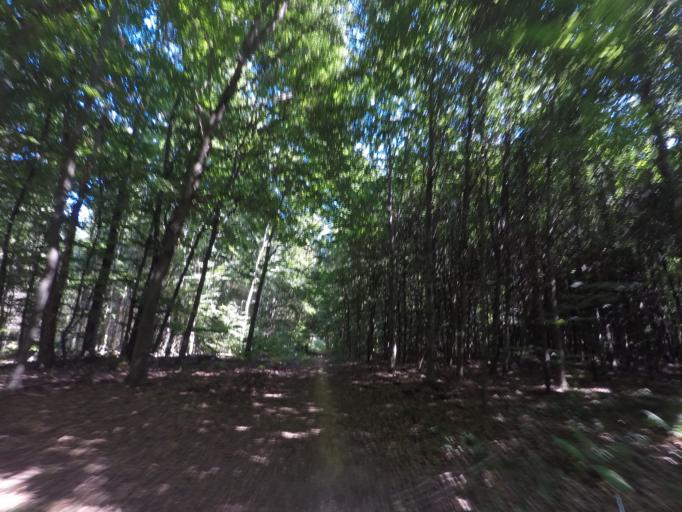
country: LU
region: Luxembourg
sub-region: Canton de Capellen
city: Kopstal
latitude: 49.6497
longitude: 6.0691
